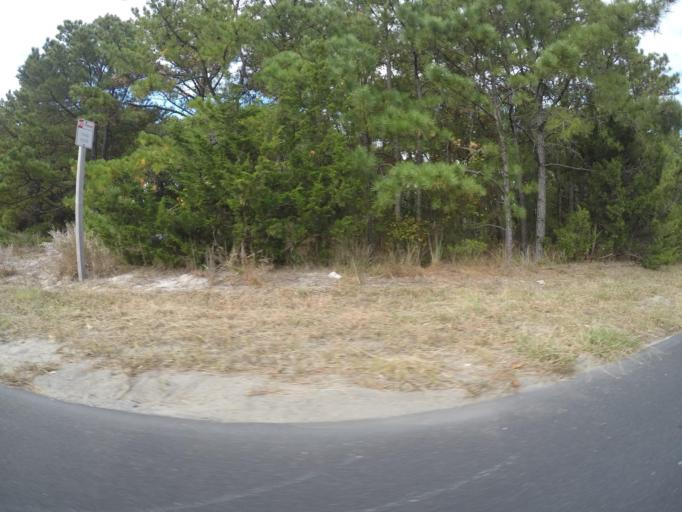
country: US
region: Delaware
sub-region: Sussex County
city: Rehoboth Beach
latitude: 38.7272
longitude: -75.0796
